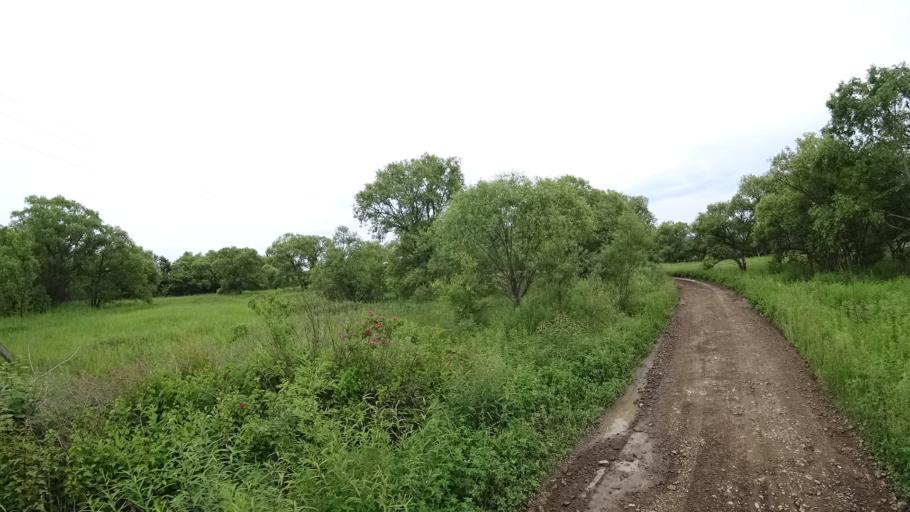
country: RU
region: Primorskiy
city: Novosysoyevka
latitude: 44.2088
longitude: 133.3283
